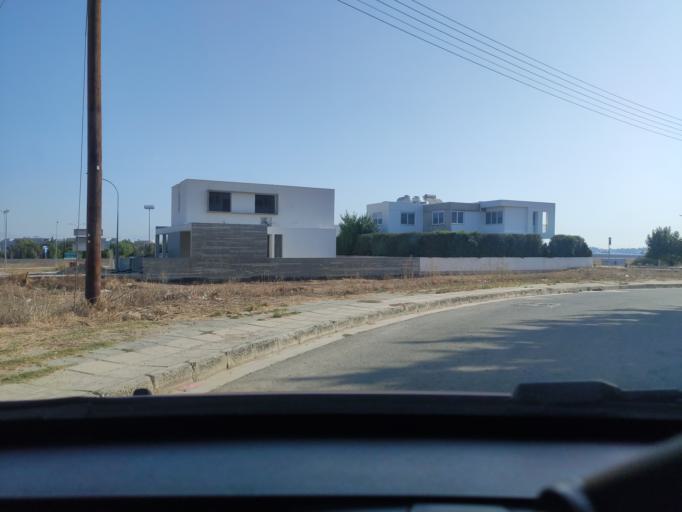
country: CY
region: Lefkosia
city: Tseri
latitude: 35.1109
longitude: 33.3581
